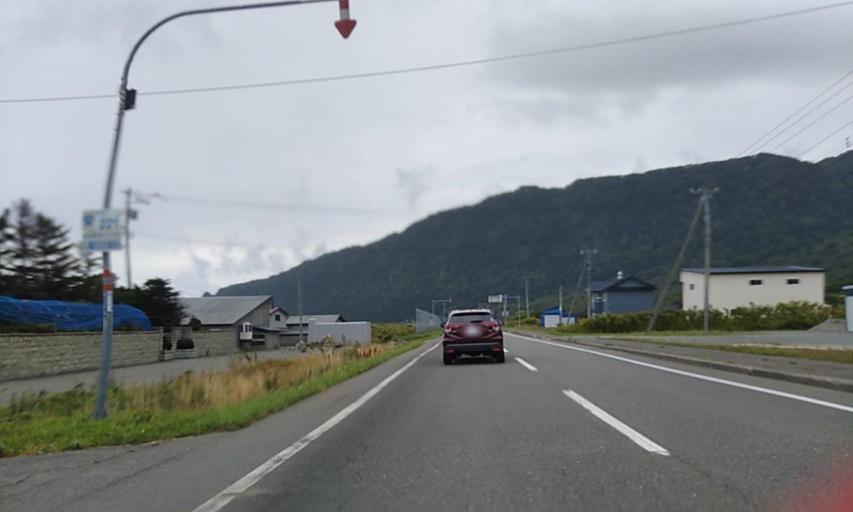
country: JP
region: Hokkaido
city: Makubetsu
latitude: 45.0686
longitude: 142.4718
